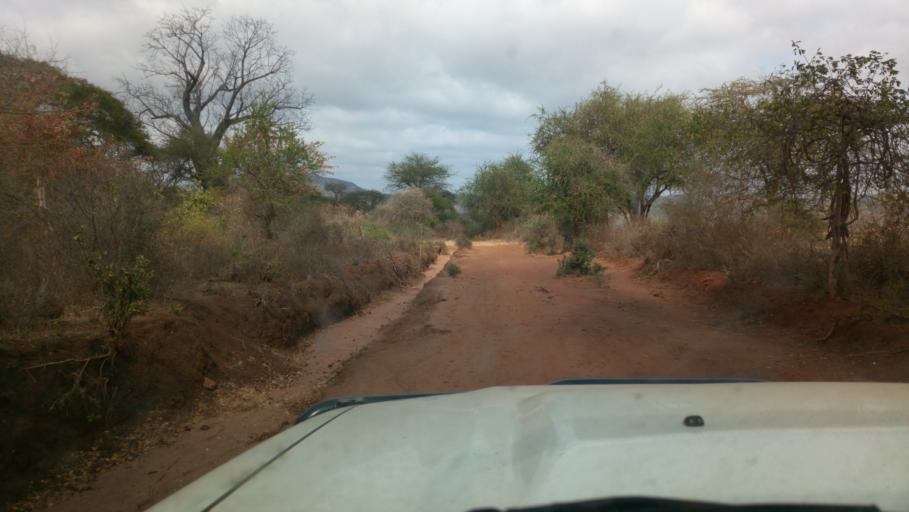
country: KE
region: Kitui
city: Kitui
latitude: -1.8617
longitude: 38.2882
